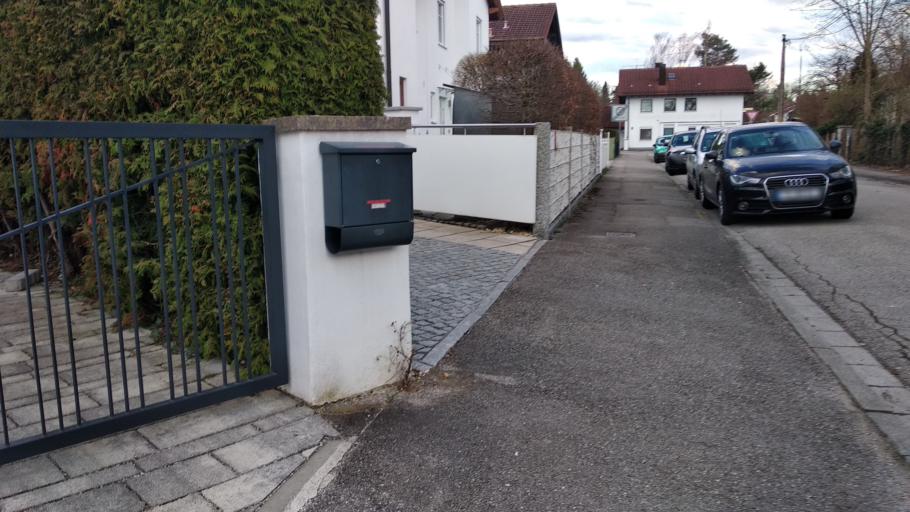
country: DE
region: Bavaria
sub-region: Upper Bavaria
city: Ottobrunn
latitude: 48.0754
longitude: 11.6849
